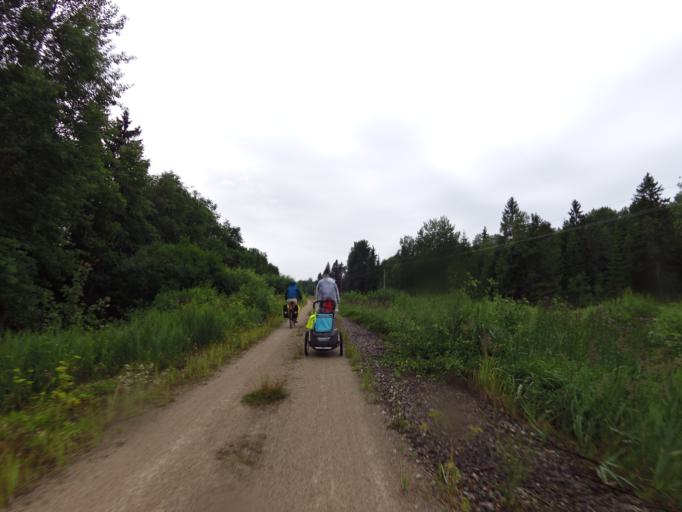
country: EE
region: Harju
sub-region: Nissi vald
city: Turba
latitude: 58.9924
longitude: 23.9580
